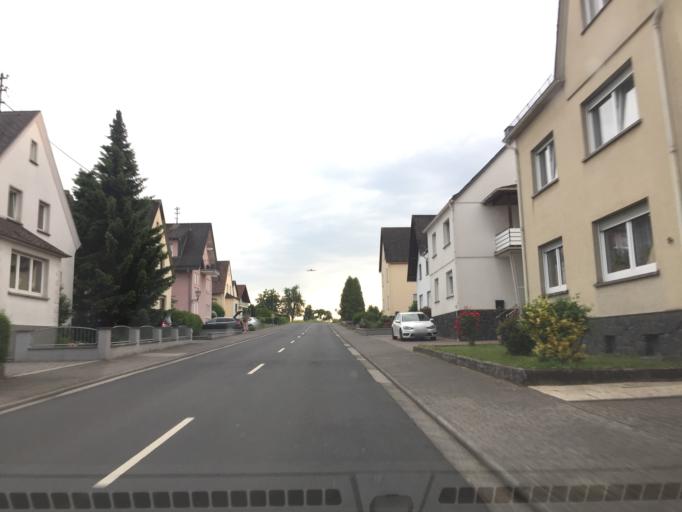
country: DE
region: Rheinland-Pfalz
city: Hundsangen
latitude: 50.4512
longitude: 7.9859
